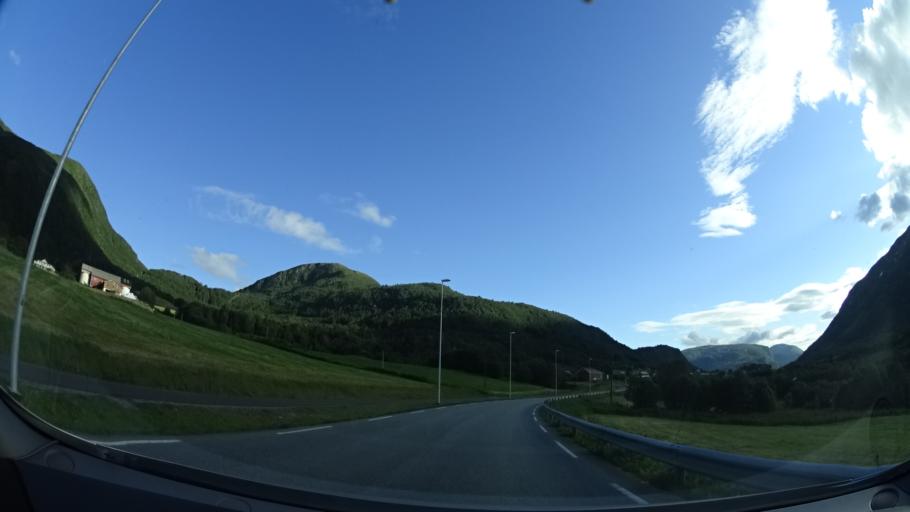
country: NO
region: More og Romsdal
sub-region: Gjemnes
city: Batnfjordsora
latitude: 62.8790
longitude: 7.6514
